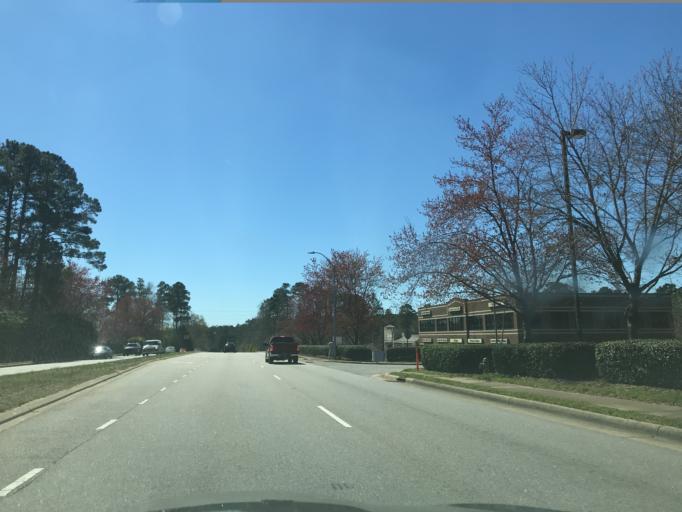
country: US
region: North Carolina
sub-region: Wake County
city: Garner
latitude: 35.7032
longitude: -78.6408
